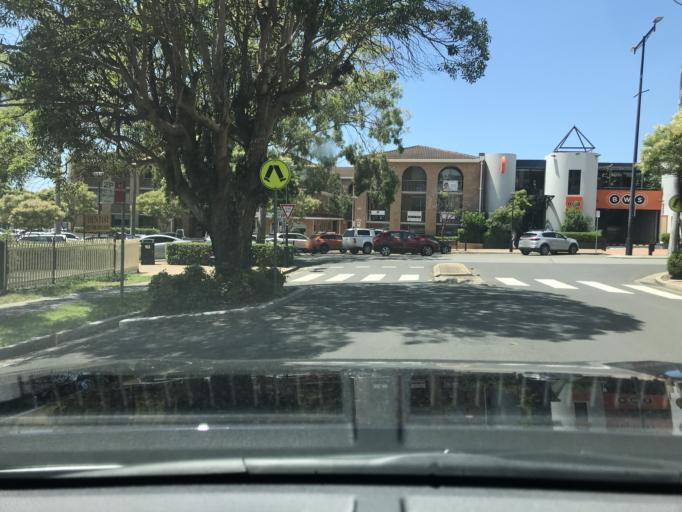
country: AU
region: New South Wales
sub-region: Canada Bay
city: Concord
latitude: -33.8551
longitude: 151.1027
